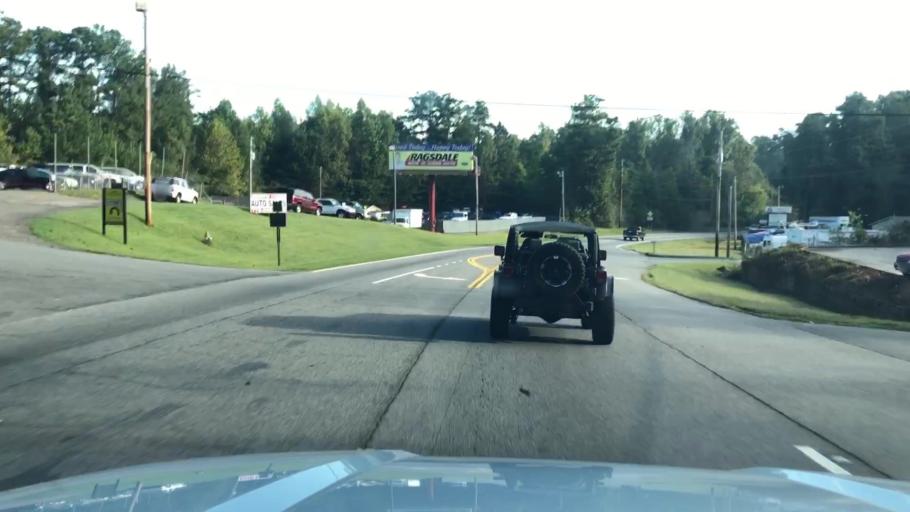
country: US
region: Georgia
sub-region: Cobb County
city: Acworth
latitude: 34.0709
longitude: -84.6843
